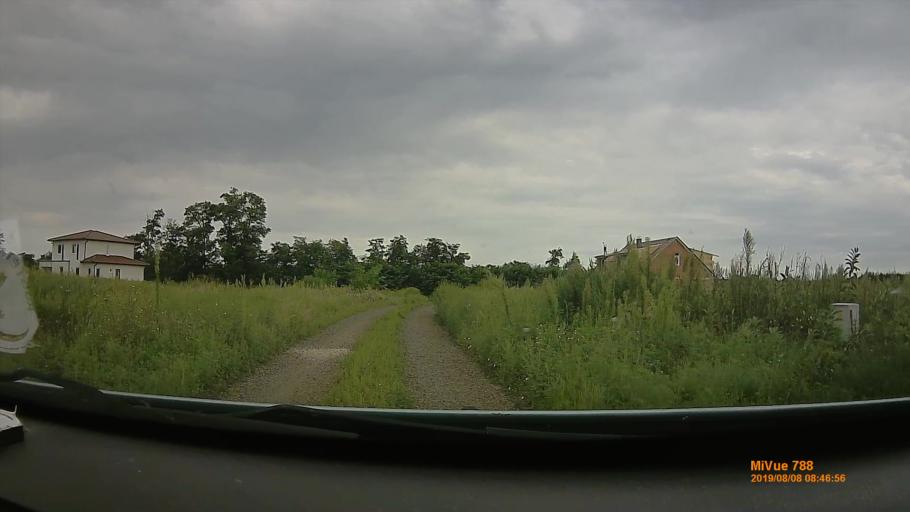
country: HU
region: Hajdu-Bihar
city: Debrecen
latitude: 47.5983
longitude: 21.6370
